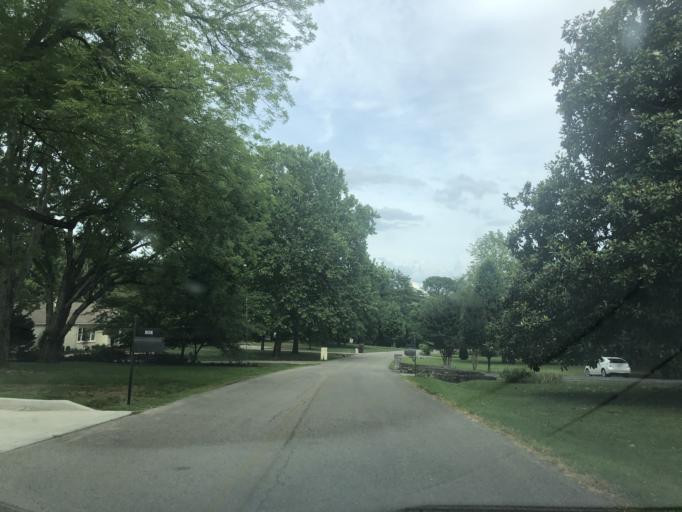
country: US
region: Tennessee
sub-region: Davidson County
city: Oak Hill
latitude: 36.0955
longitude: -86.7822
